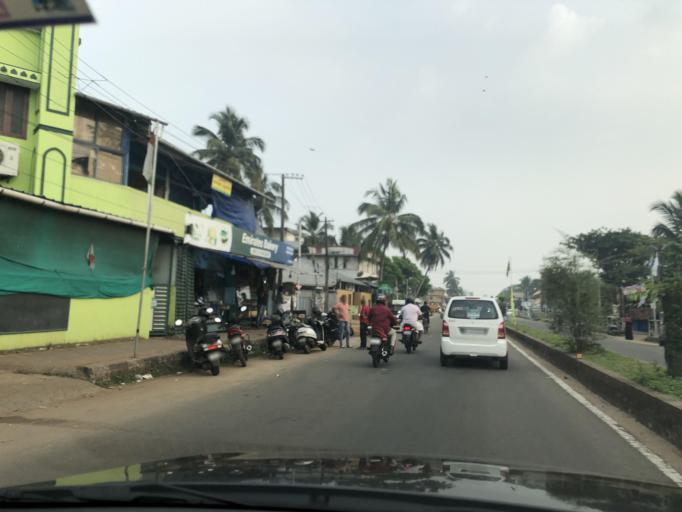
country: IN
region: Kerala
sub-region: Kozhikode
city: Kozhikode
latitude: 11.2713
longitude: 75.7655
